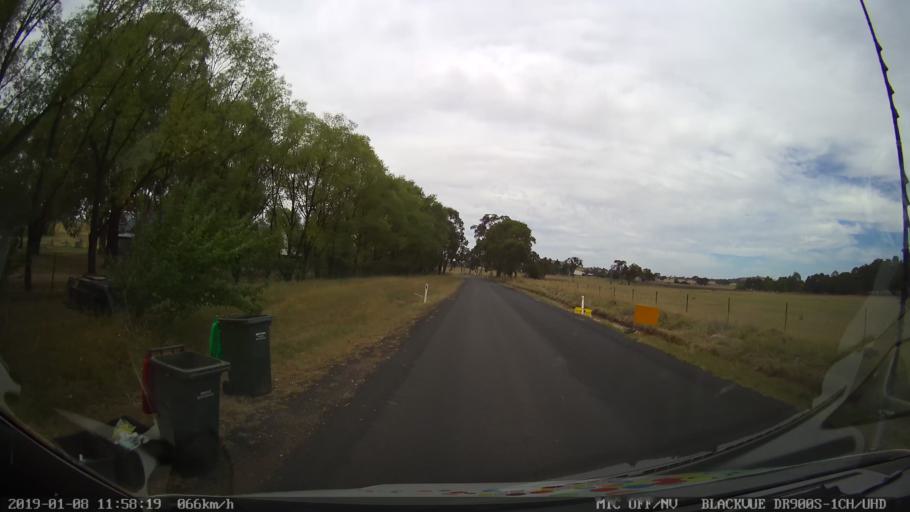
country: AU
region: New South Wales
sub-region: Armidale Dumaresq
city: Armidale
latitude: -30.4560
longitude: 151.5740
